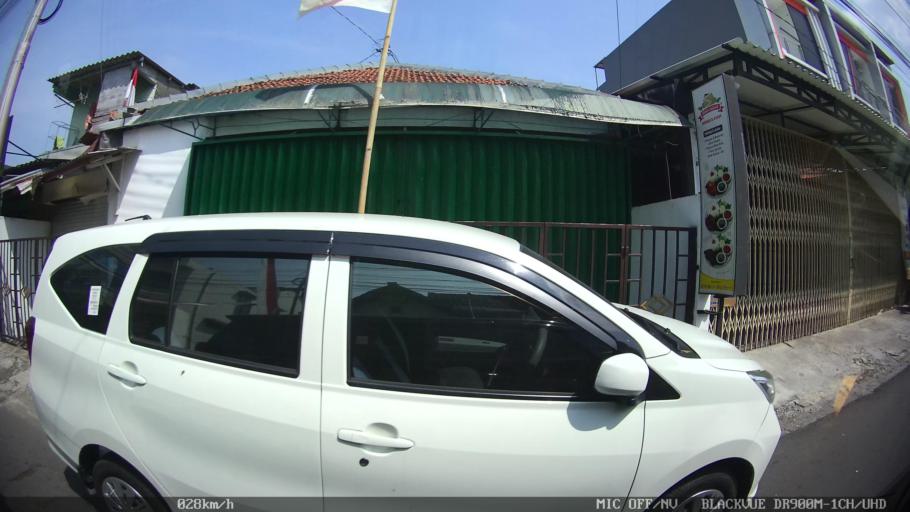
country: ID
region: Daerah Istimewa Yogyakarta
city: Yogyakarta
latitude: -7.7859
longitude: 110.3629
